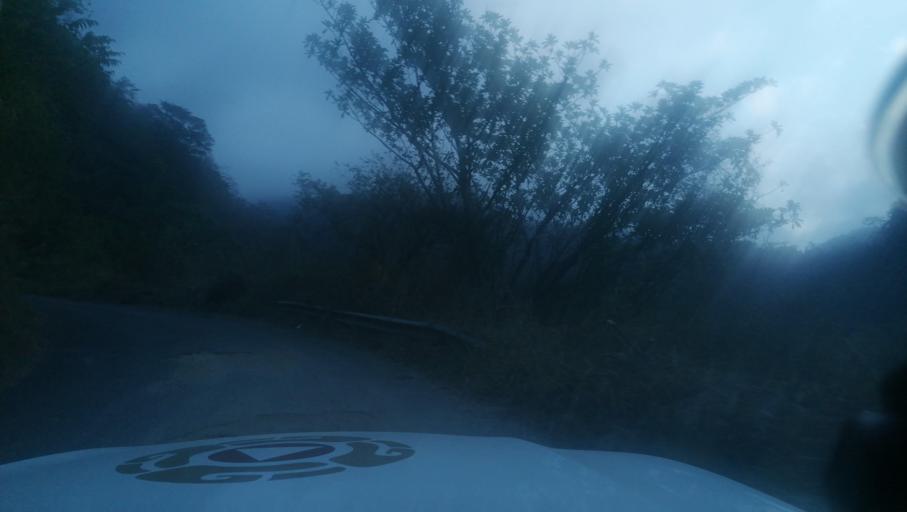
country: MX
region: Chiapas
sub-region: Cacahoatan
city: Benito Juarez
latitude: 15.1384
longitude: -92.1982
